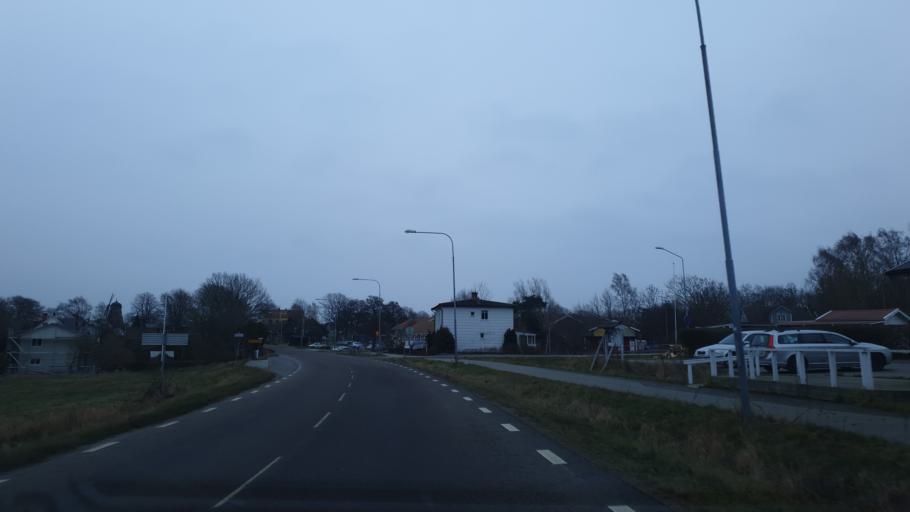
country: SE
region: Blekinge
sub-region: Karlskrona Kommun
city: Sturko
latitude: 56.1132
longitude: 15.6752
